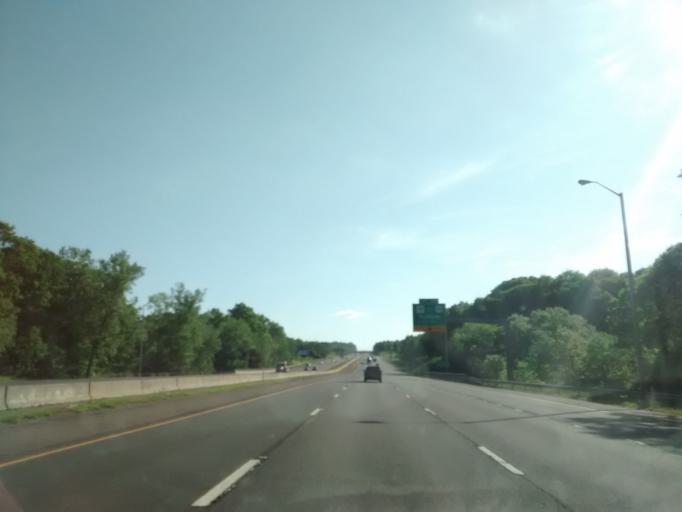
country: US
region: Connecticut
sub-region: Tolland County
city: Stafford Springs
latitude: 41.8911
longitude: -72.3016
